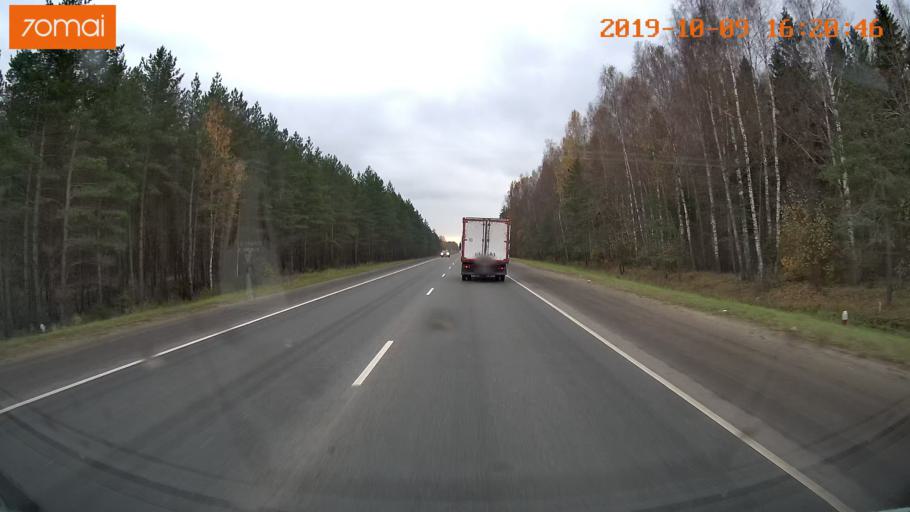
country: RU
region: Kostroma
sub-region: Kostromskoy Rayon
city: Kostroma
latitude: 57.7021
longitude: 40.8913
